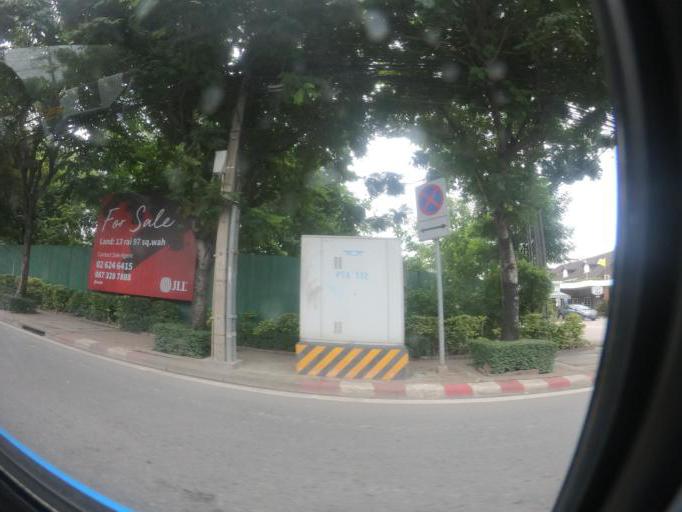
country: TH
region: Bangkok
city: Watthana
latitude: 13.7386
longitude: 100.6069
